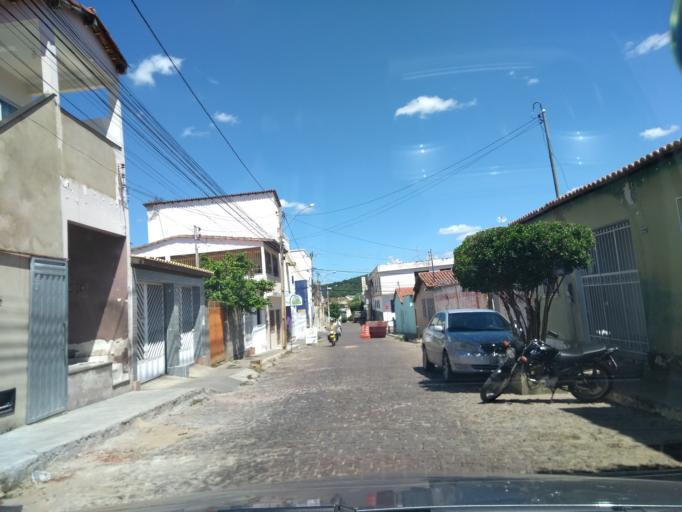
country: BR
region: Bahia
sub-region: Brumado
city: Brumado
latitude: -14.2071
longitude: -41.6701
